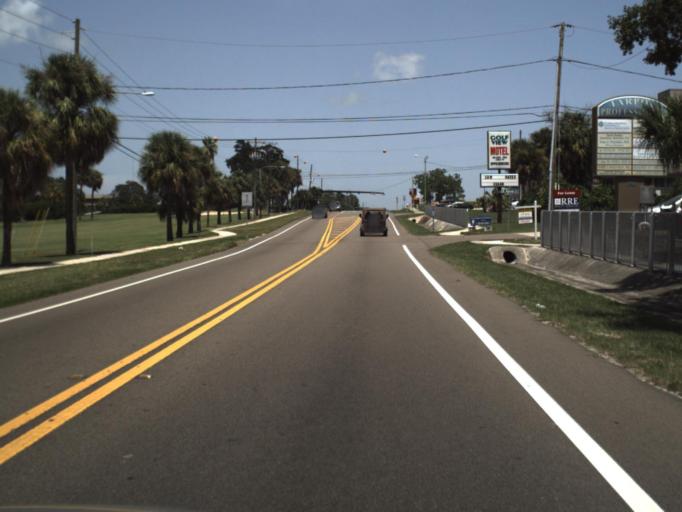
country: US
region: Florida
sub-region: Pinellas County
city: Tarpon Springs
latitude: 28.1308
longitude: -82.7588
